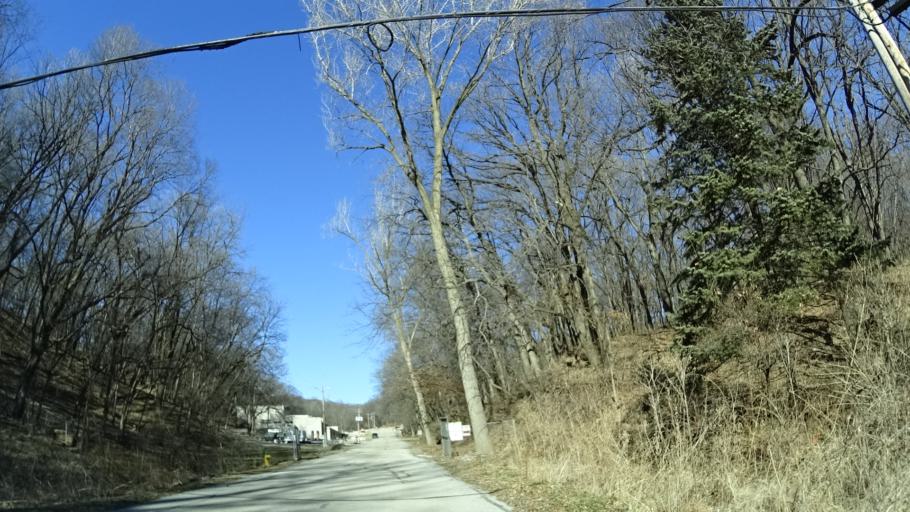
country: US
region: Nebraska
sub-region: Sarpy County
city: Bellevue
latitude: 41.1574
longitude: -95.8949
